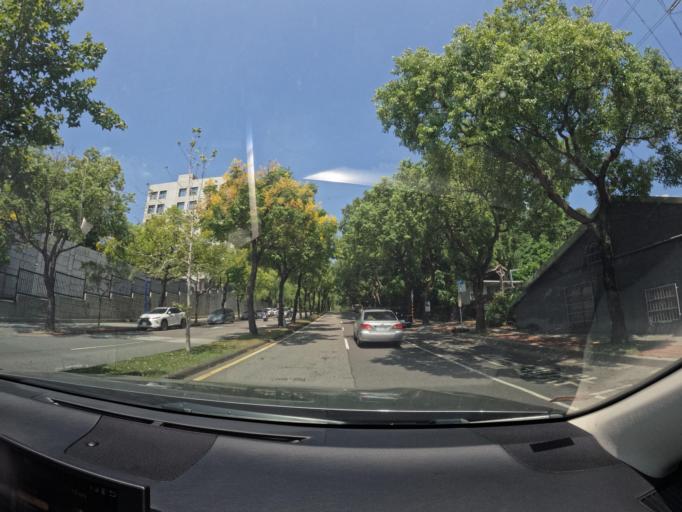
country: TW
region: Taipei
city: Taipei
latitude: 25.1142
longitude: 121.5392
